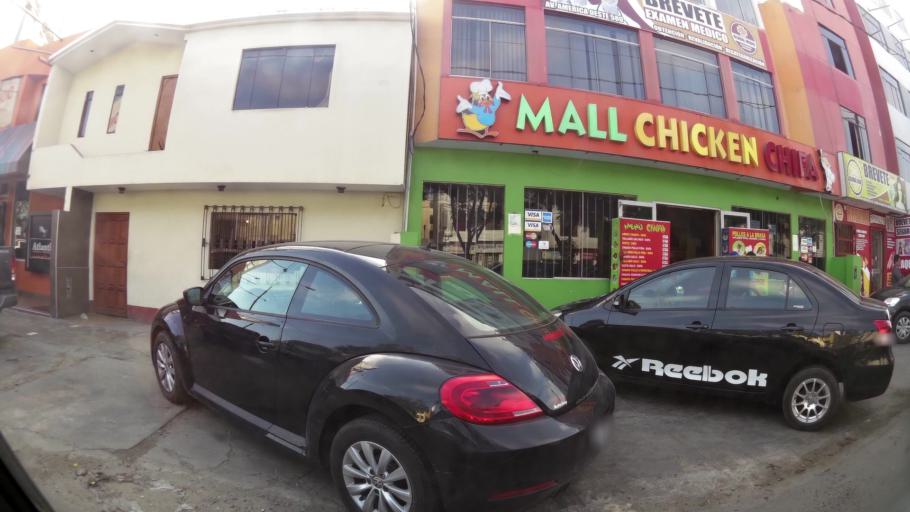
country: PE
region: La Libertad
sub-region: Provincia de Trujillo
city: Trujillo
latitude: -8.1009
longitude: -79.0443
